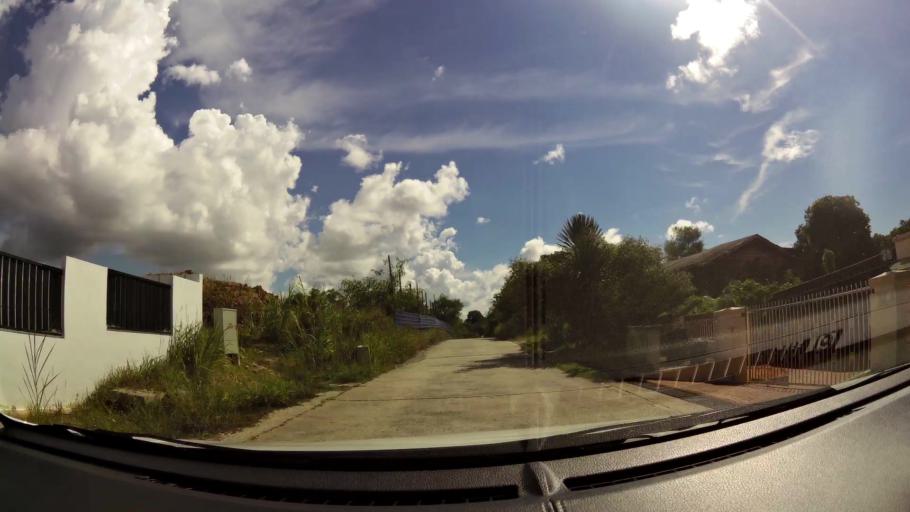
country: BN
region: Brunei and Muara
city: Bandar Seri Begawan
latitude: 4.9532
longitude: 114.9438
